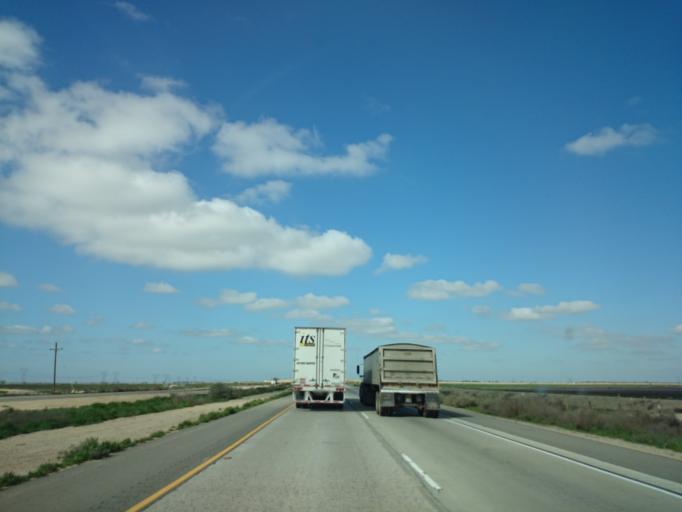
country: US
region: California
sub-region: Kern County
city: Rosedale
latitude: 35.3253
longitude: -119.2940
